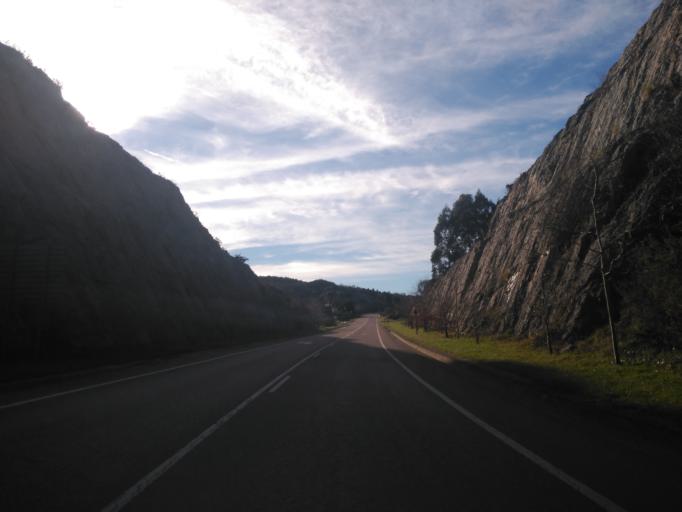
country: ES
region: Cantabria
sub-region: Provincia de Cantabria
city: Comillas
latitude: 43.3616
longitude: -4.2674
